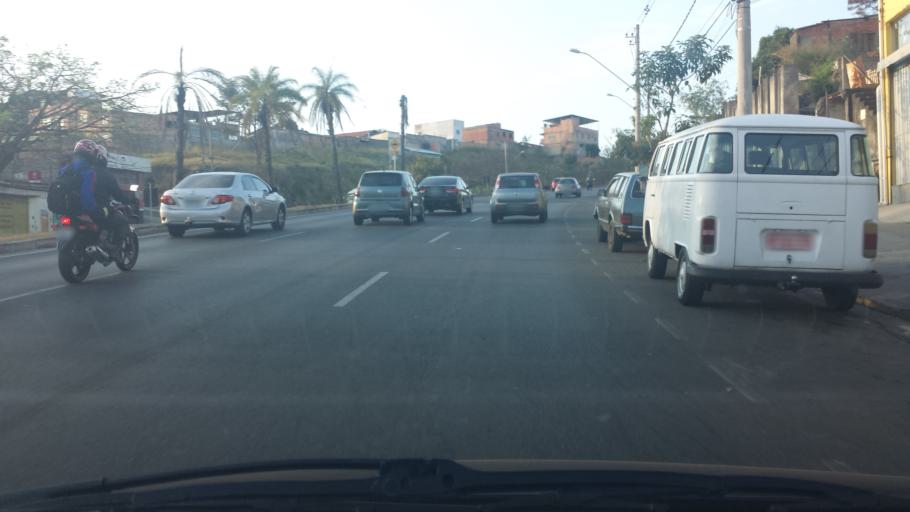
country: BR
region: Minas Gerais
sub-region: Belo Horizonte
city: Belo Horizonte
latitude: -19.8957
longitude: -43.9923
